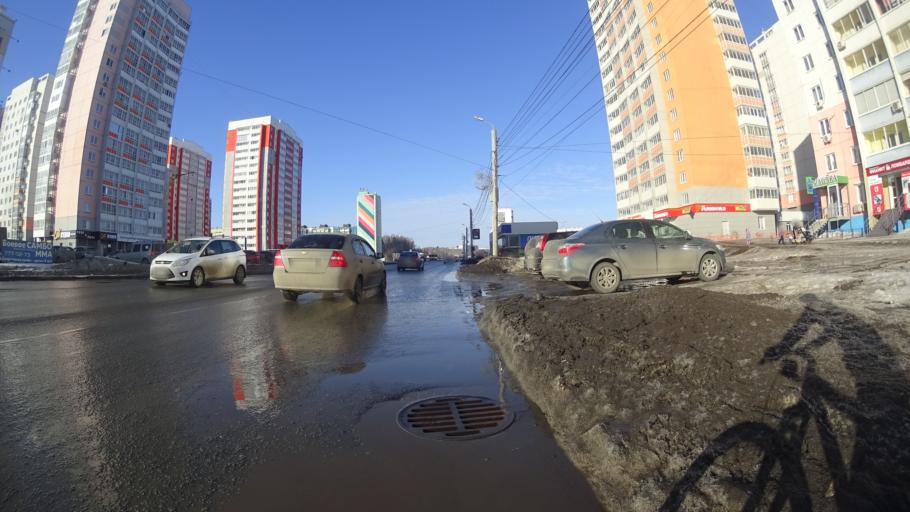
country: RU
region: Chelyabinsk
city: Roshchino
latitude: 55.2081
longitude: 61.2844
